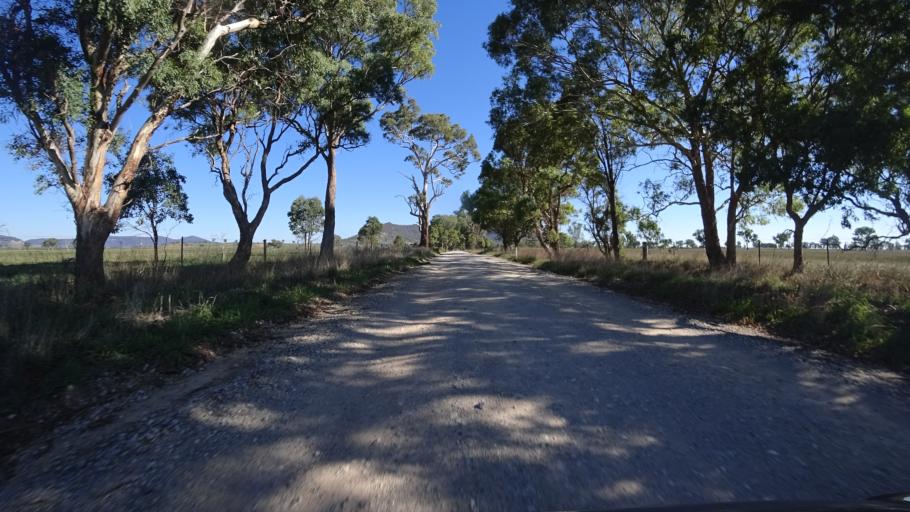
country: AU
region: New South Wales
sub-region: Mid-Western Regional
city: Kandos
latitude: -32.8218
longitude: 150.0220
